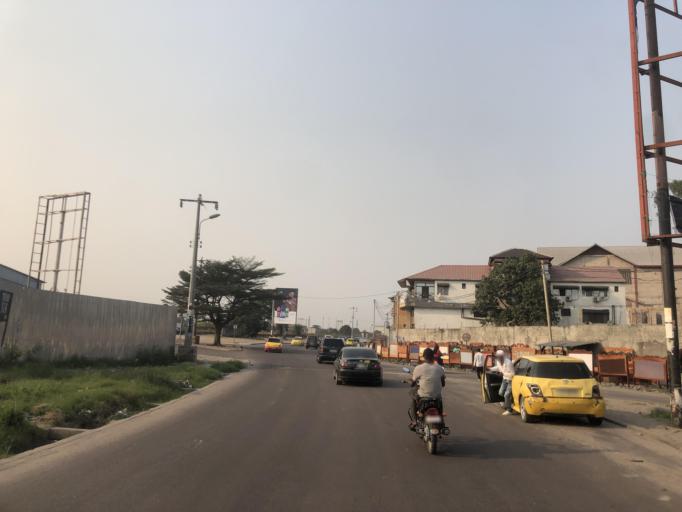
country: CD
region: Kinshasa
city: Kinshasa
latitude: -4.3294
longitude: 15.3299
